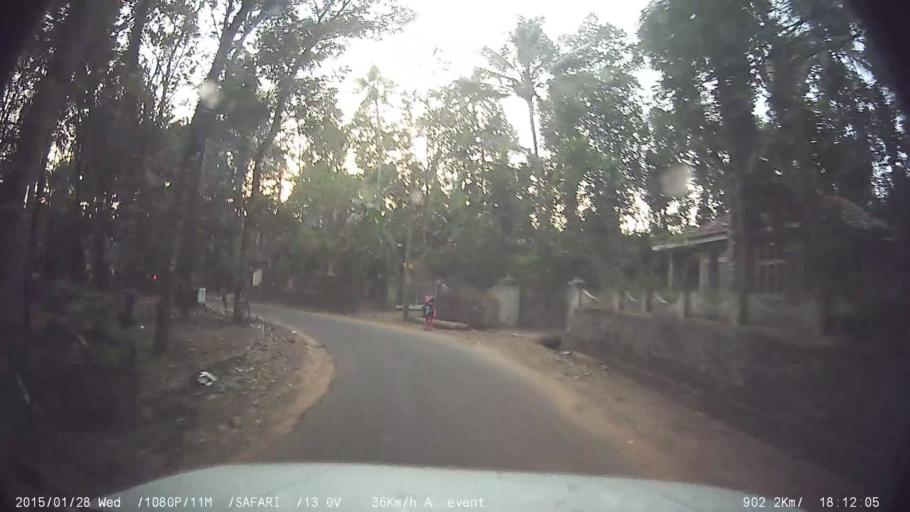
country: IN
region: Kerala
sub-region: Kottayam
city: Palackattumala
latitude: 9.7533
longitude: 76.5665
